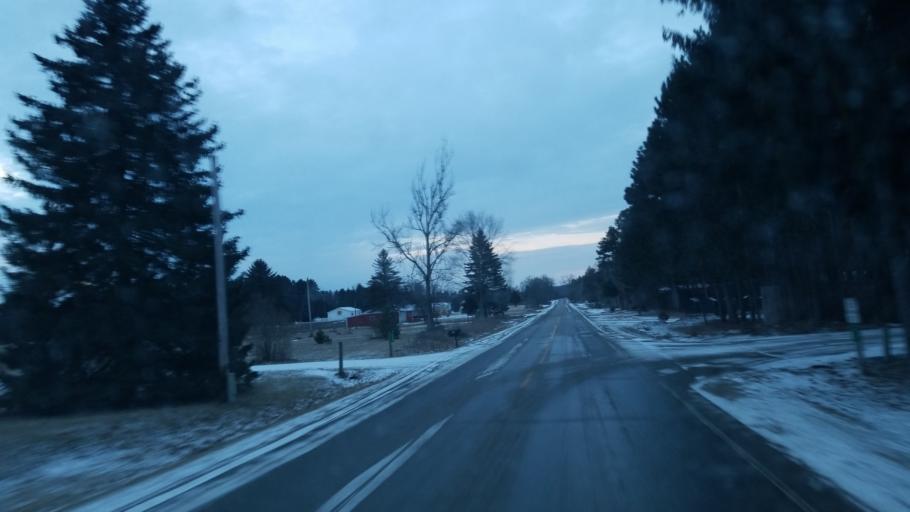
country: US
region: Michigan
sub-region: Osceola County
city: Reed City
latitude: 43.8368
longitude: -85.4242
